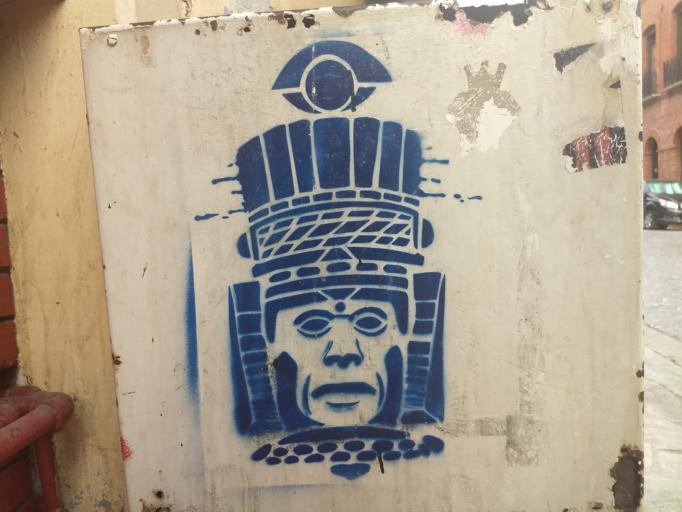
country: MX
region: Nuevo Leon
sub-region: Monterrey
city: Monterrey
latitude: 25.6650
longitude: -100.3088
